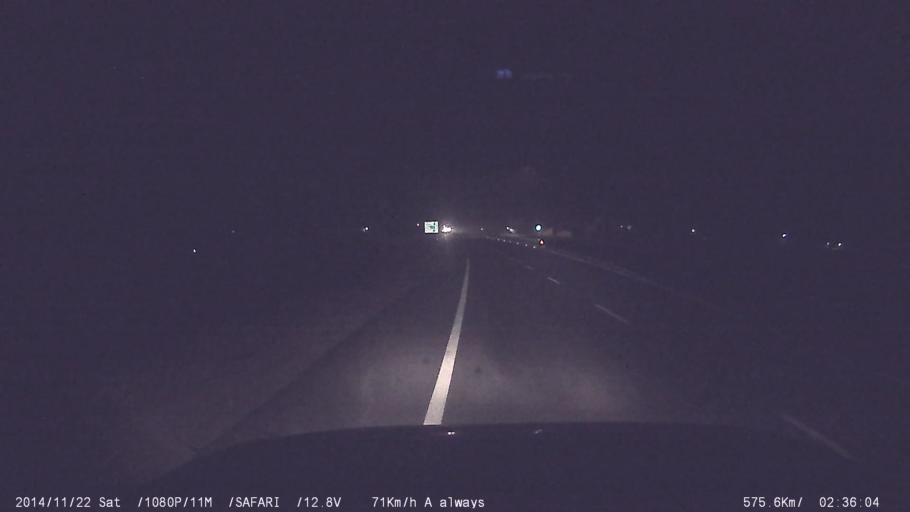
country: IN
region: Tamil Nadu
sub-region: Salem
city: Belur
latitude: 11.6538
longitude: 78.3821
